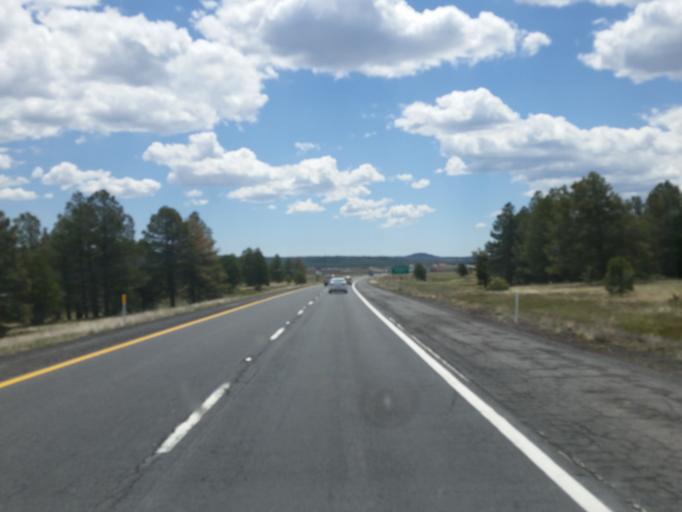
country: US
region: Arizona
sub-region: Coconino County
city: Parks
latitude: 35.2450
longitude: -111.8428
